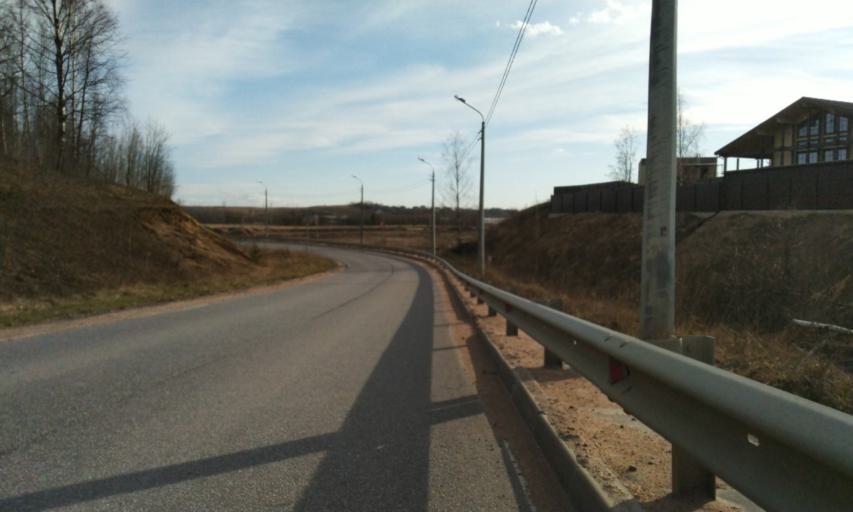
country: RU
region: Leningrad
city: Bugry
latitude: 60.1157
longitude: 30.4245
